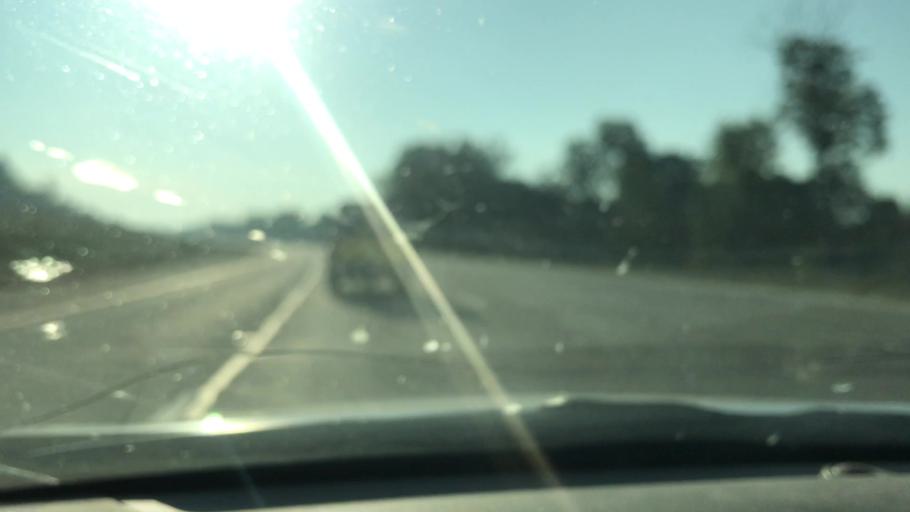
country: US
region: Michigan
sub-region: Livingston County
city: Howell
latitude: 42.6115
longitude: -83.9858
